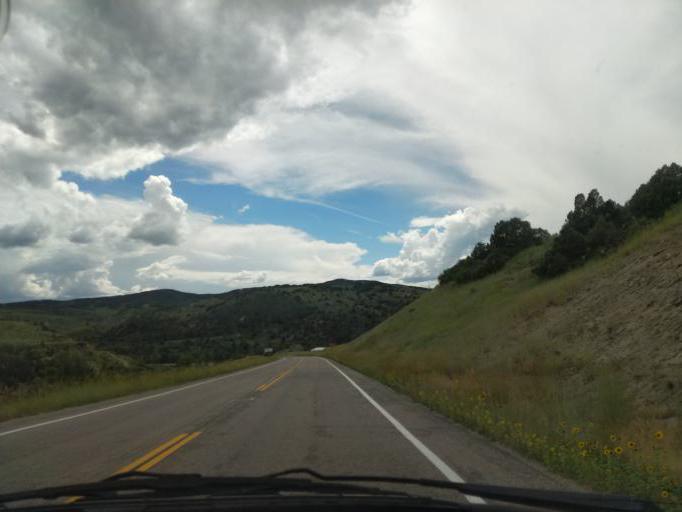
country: US
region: Colorado
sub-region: Delta County
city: Paonia
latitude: 39.0821
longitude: -107.3658
